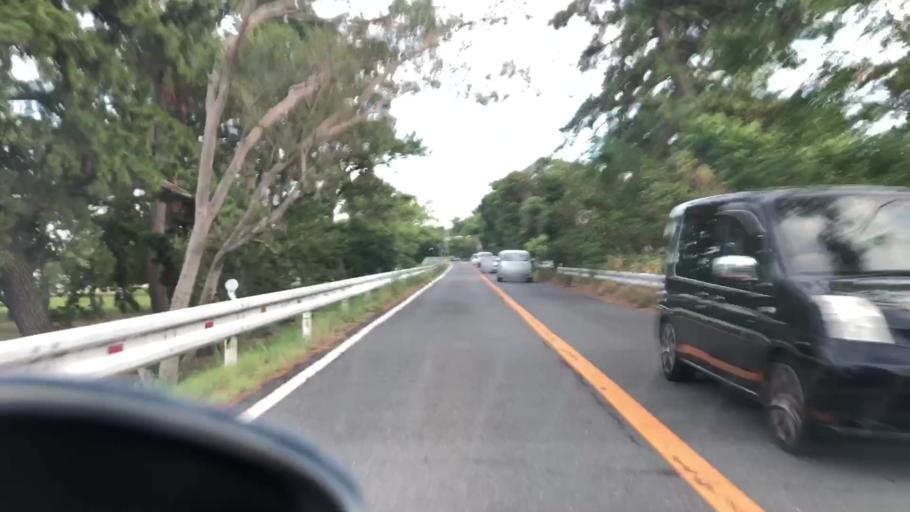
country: JP
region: Hyogo
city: Itami
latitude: 34.7551
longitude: 135.3723
